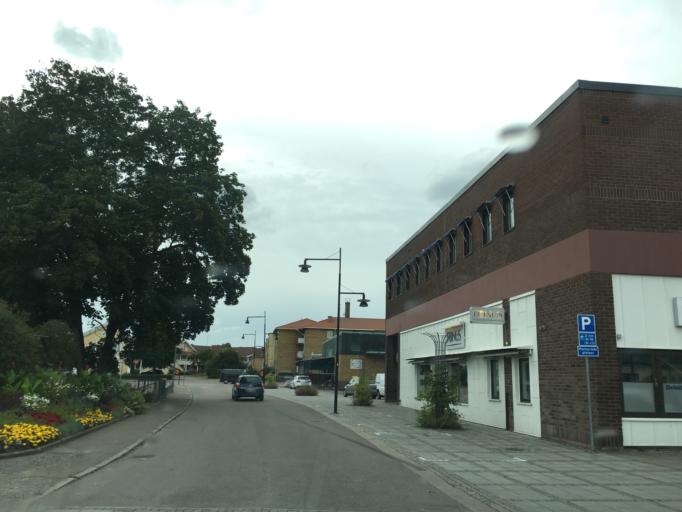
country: SE
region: Kalmar
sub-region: Nybro Kommun
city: Nybro
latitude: 56.7435
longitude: 15.9066
